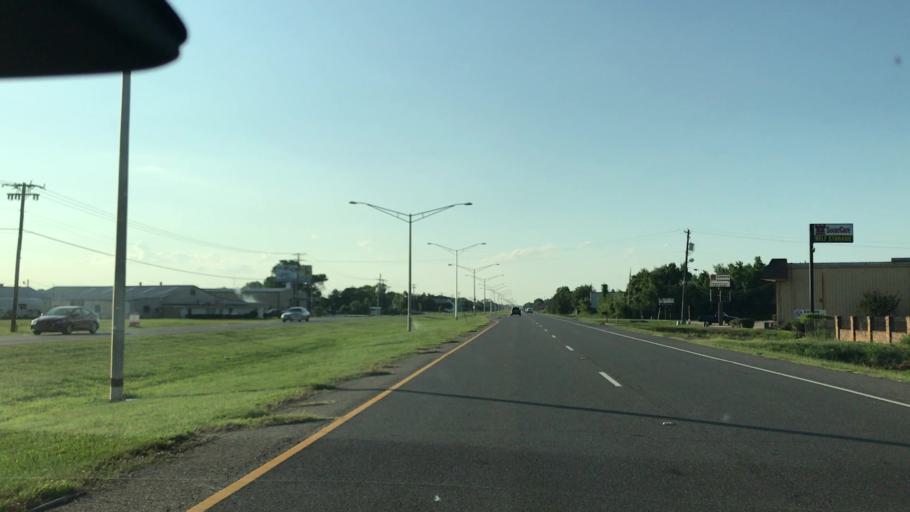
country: US
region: Louisiana
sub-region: Bossier Parish
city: Bossier City
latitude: 32.4040
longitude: -93.6957
